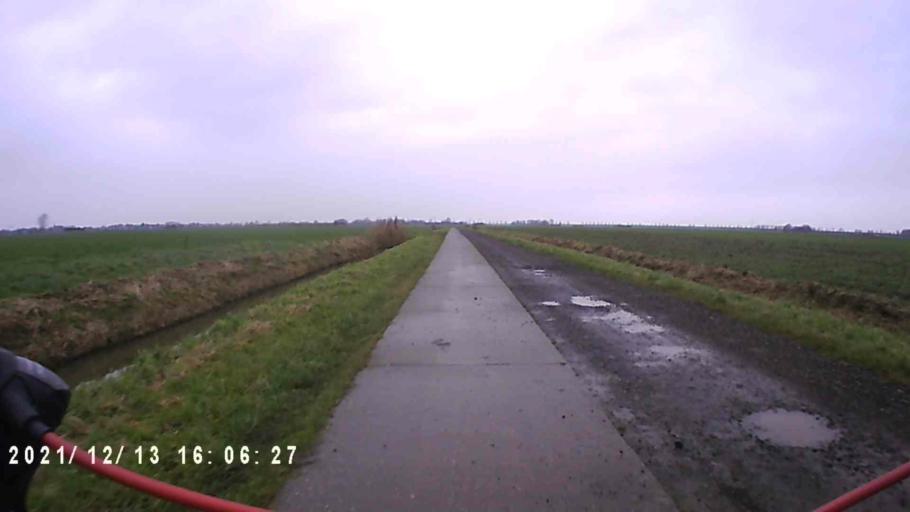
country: NL
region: Groningen
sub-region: Gemeente Appingedam
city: Appingedam
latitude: 53.3414
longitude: 6.8785
